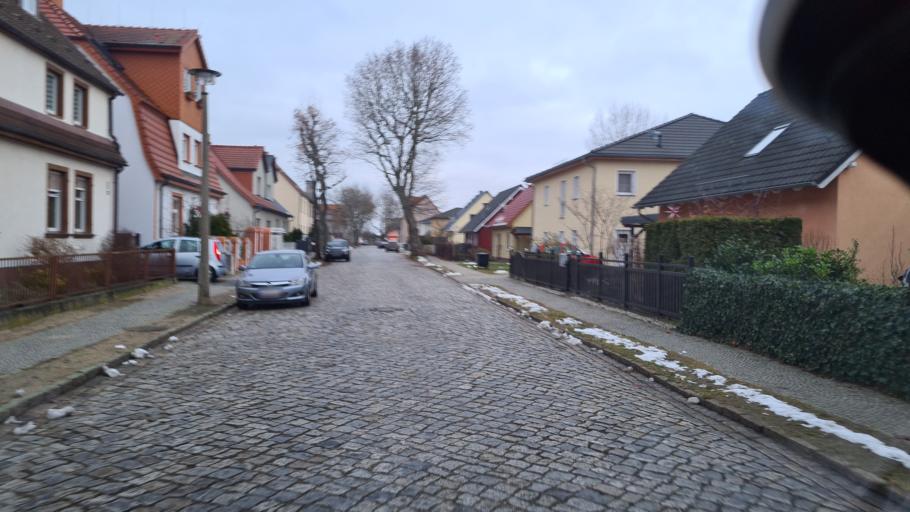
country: DE
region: Brandenburg
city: Eisenhuettenstadt
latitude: 52.1448
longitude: 14.6622
